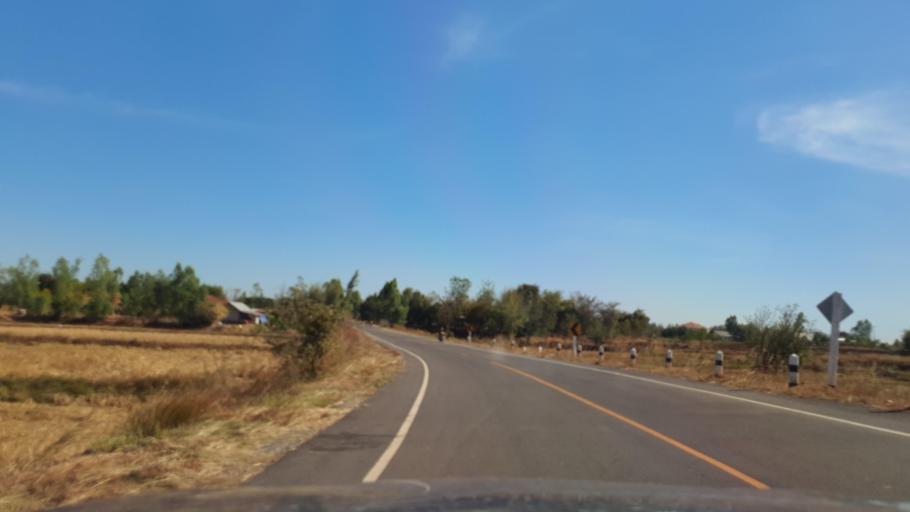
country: TH
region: Kalasin
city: Khao Wong
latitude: 16.7270
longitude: 104.0996
